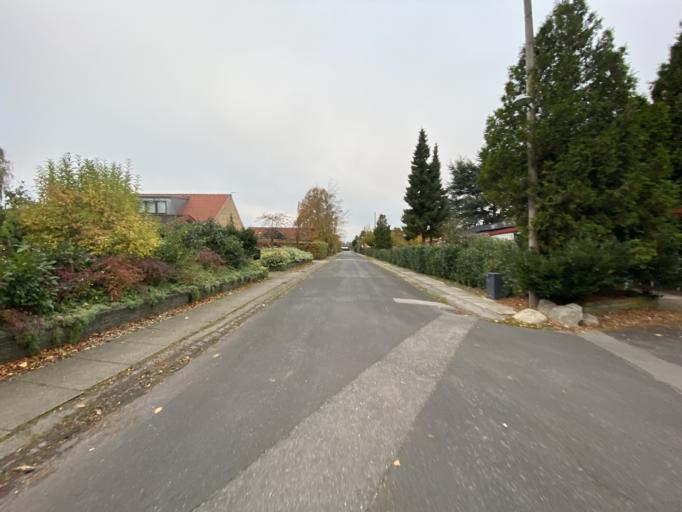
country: DK
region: Capital Region
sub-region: Dragor Kommune
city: Dragor
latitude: 55.5953
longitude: 12.6660
